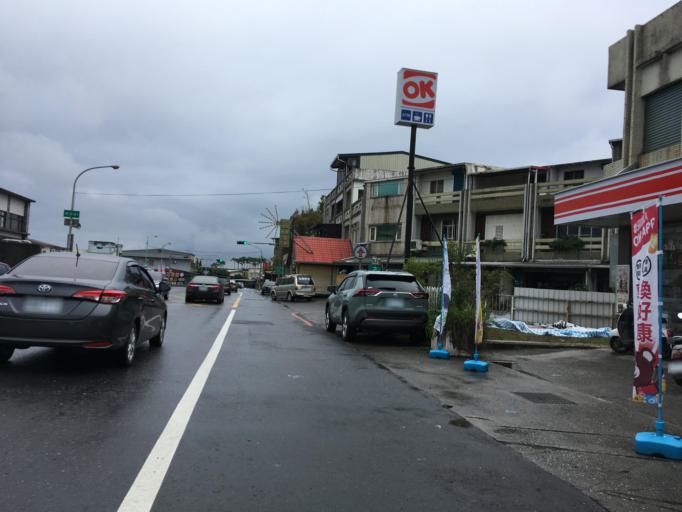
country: TW
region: Taiwan
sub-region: Yilan
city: Yilan
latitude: 24.6564
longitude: 121.7600
